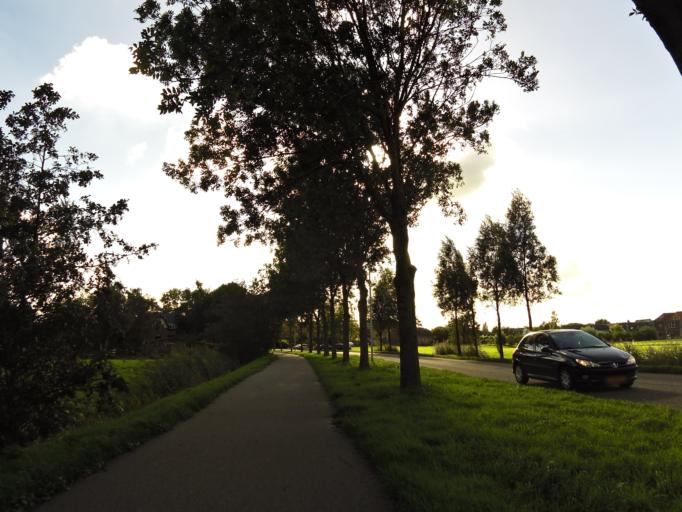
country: NL
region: South Holland
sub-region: Gemeente Leiderdorp
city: Leiderdorp
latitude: 52.1430
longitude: 4.5351
